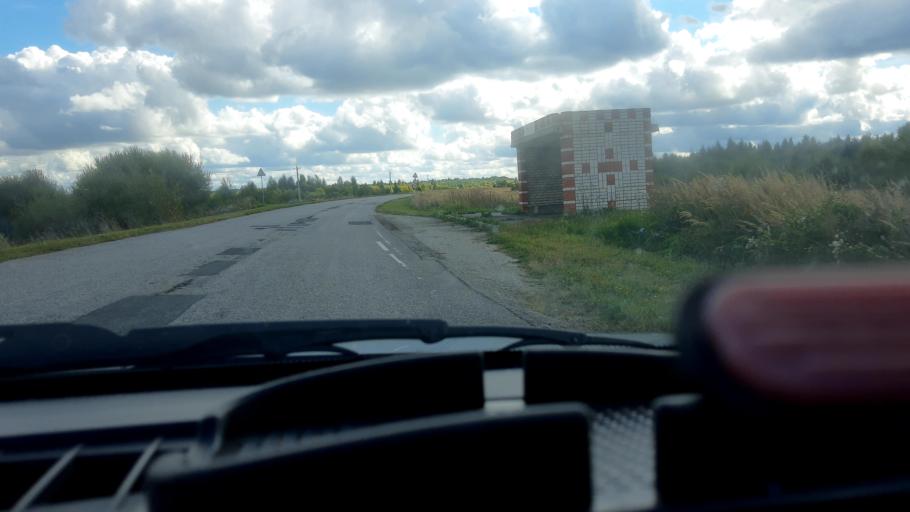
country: RU
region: Mariy-El
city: Kilemary
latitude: 56.9411
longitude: 46.6871
